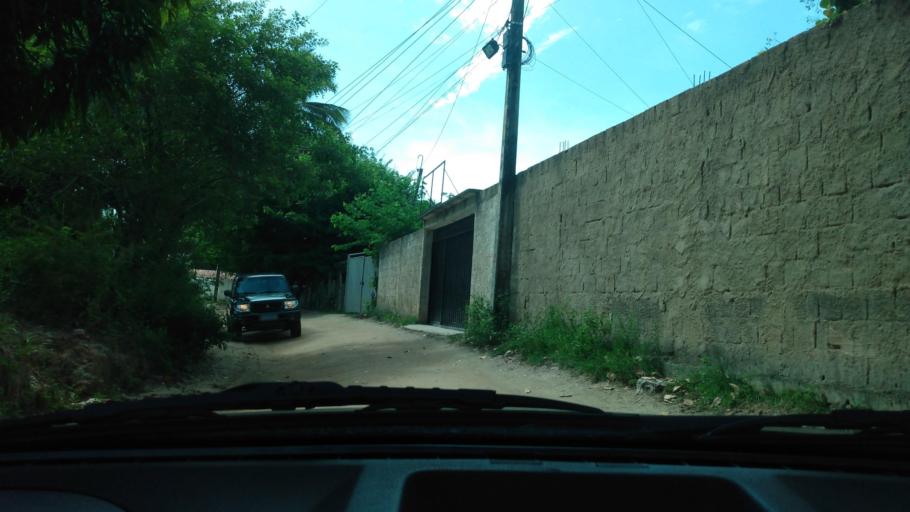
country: BR
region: Pernambuco
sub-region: Cabo De Santo Agostinho
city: Cabo
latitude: -8.3521
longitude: -34.9638
